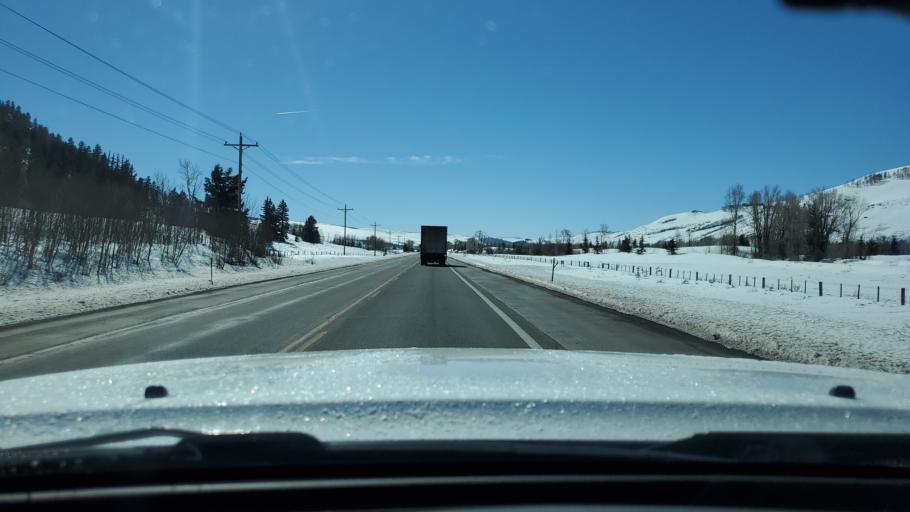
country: US
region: Colorado
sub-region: Gunnison County
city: Crested Butte
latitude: 38.7790
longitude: -106.8695
